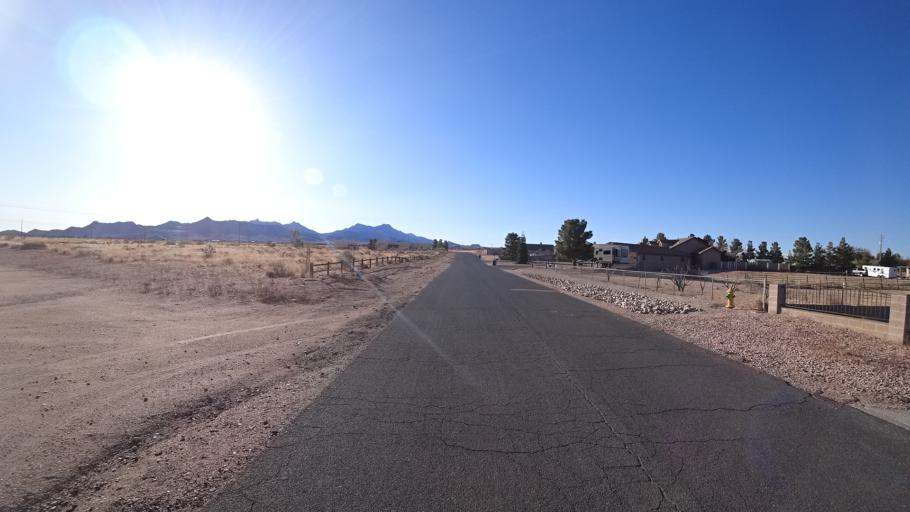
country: US
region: Arizona
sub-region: Mohave County
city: Kingman
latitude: 35.2050
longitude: -113.9953
